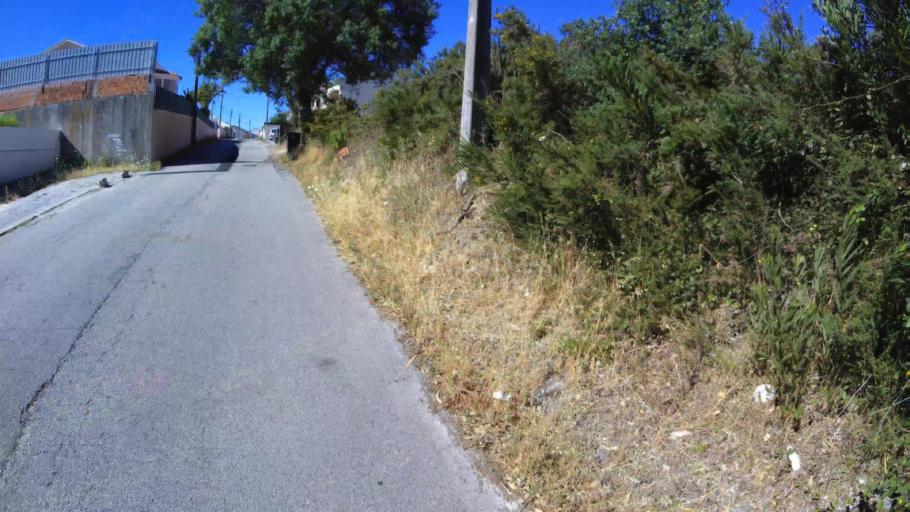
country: PT
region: Aveiro
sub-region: Aveiro
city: Aveiro
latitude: 40.6652
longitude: -8.6194
